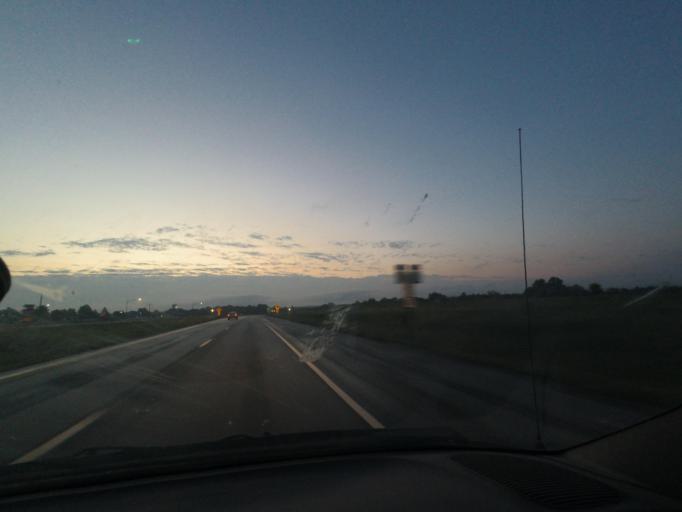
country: US
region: Missouri
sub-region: Linn County
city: Brookfield
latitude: 39.7799
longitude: -93.1057
